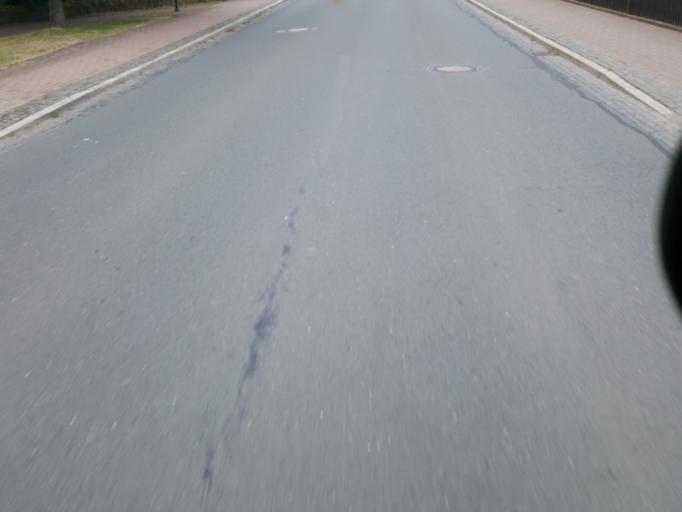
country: DE
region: Lower Saxony
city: Rehburg-Loccum
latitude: 52.4384
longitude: 9.1853
